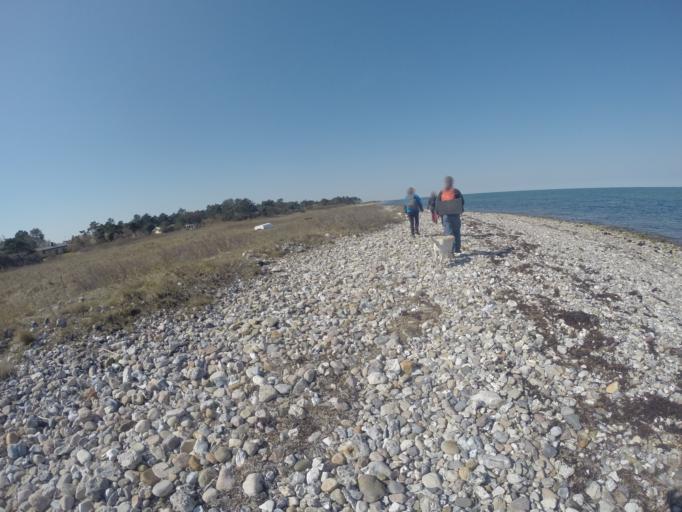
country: DK
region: Zealand
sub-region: Kalundborg Kommune
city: Gorlev
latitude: 55.5369
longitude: 11.1246
